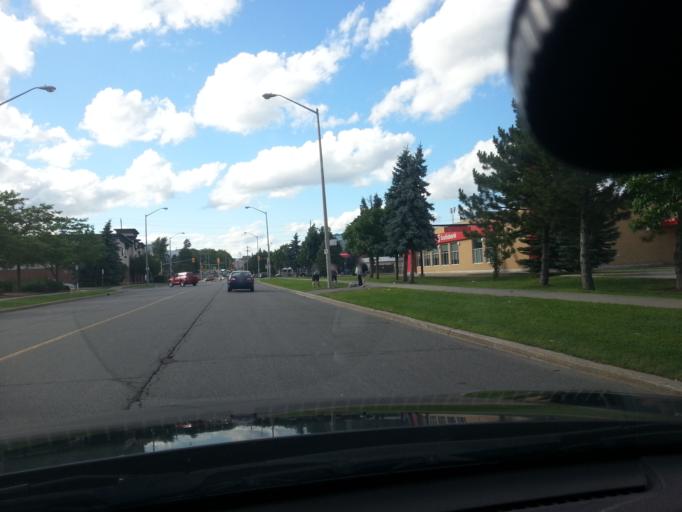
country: CA
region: Ontario
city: Ottawa
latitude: 45.4321
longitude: -75.6122
